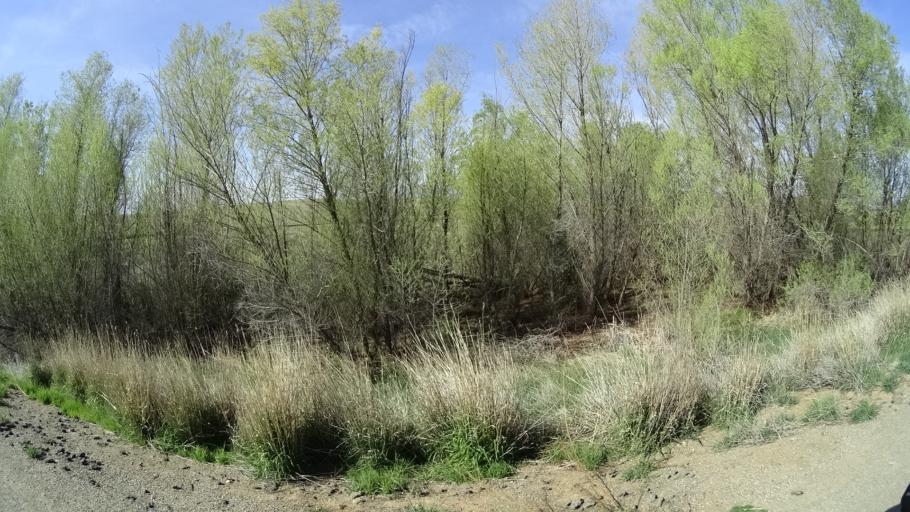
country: US
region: California
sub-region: Glenn County
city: Willows
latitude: 39.6118
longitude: -122.2872
